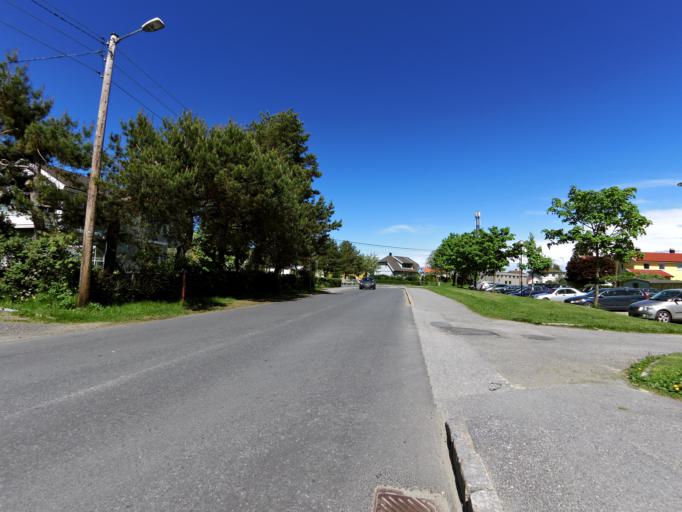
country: NO
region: Ostfold
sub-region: Fredrikstad
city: Fredrikstad
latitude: 59.2321
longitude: 10.9724
